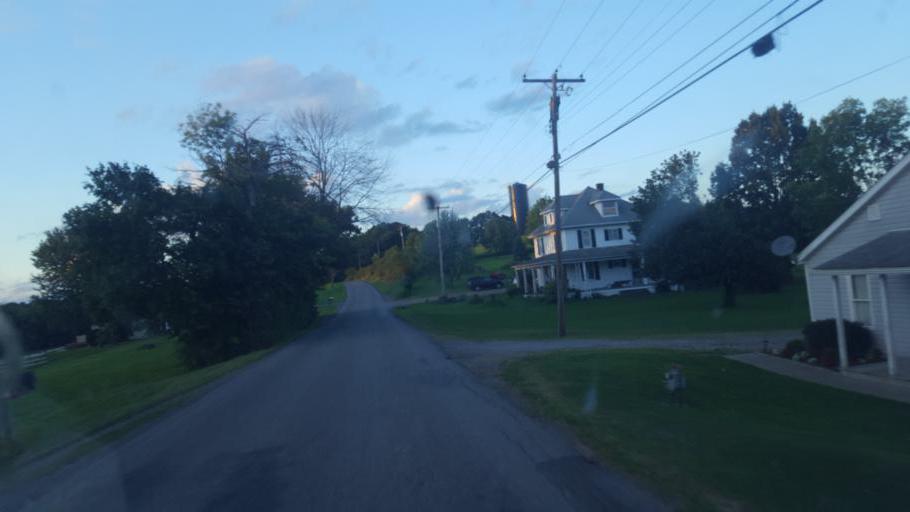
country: US
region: Pennsylvania
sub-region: Clarion County
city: Knox
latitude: 41.2221
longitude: -79.5410
